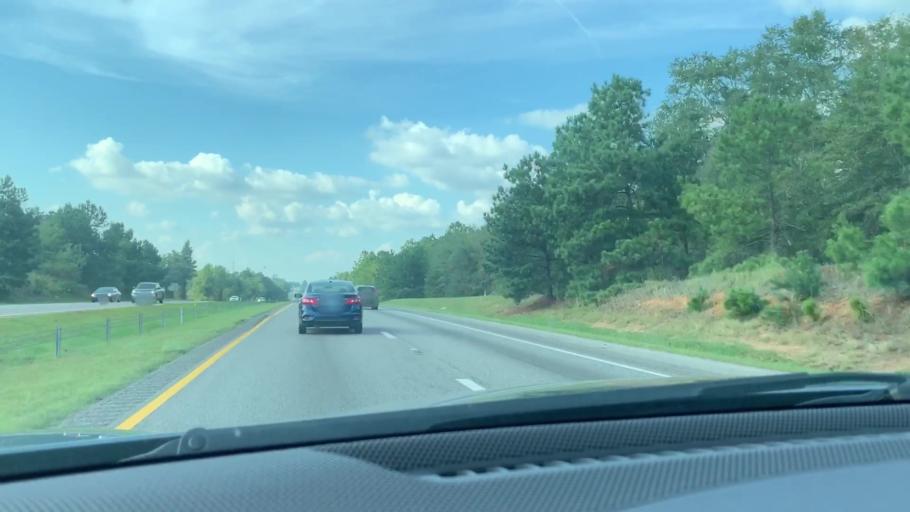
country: US
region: South Carolina
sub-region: Calhoun County
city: Saint Matthews
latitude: 33.6185
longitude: -80.8681
